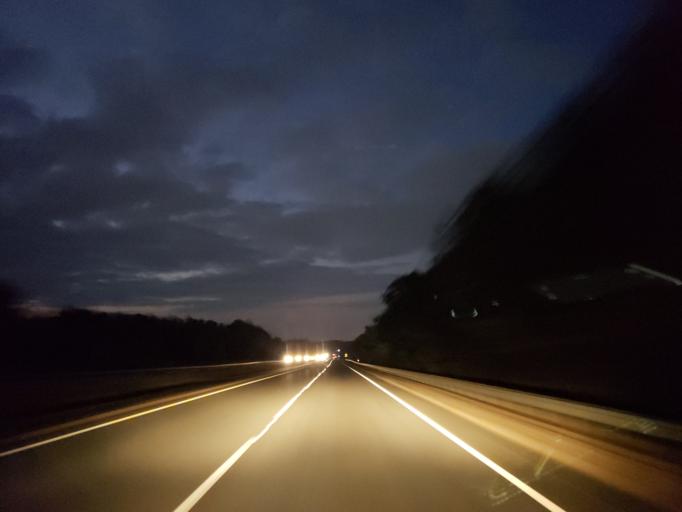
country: US
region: Georgia
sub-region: Polk County
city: Rockmart
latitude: 33.9819
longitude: -85.0132
